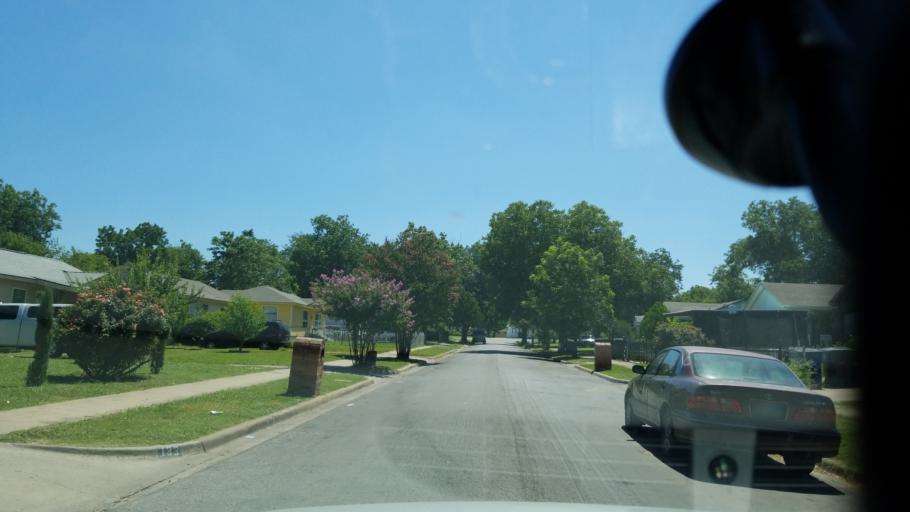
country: US
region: Texas
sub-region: Dallas County
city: Cockrell Hill
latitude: 32.7123
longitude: -96.8246
